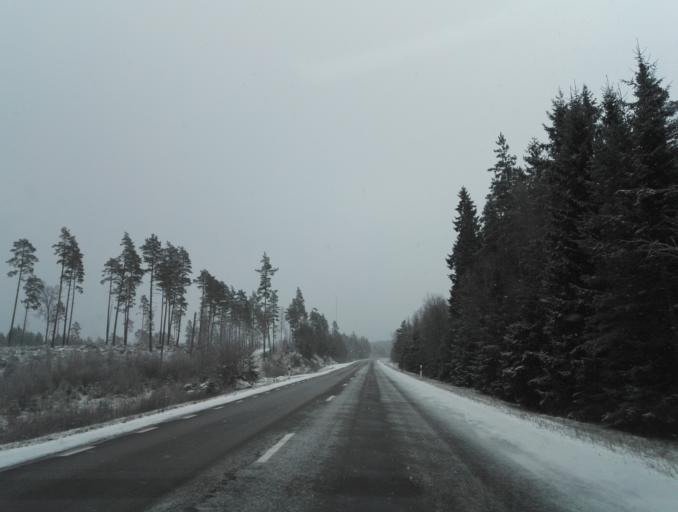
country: SE
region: Kronoberg
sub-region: Uppvidinge Kommun
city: Lenhovda
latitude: 56.9268
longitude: 15.3524
